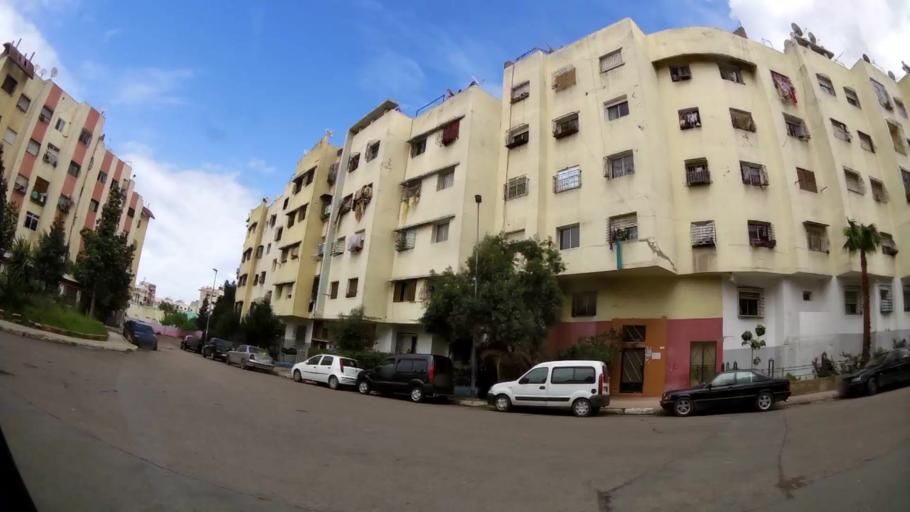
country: MA
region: Grand Casablanca
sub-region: Mediouna
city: Tit Mellil
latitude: 33.6005
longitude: -7.4903
